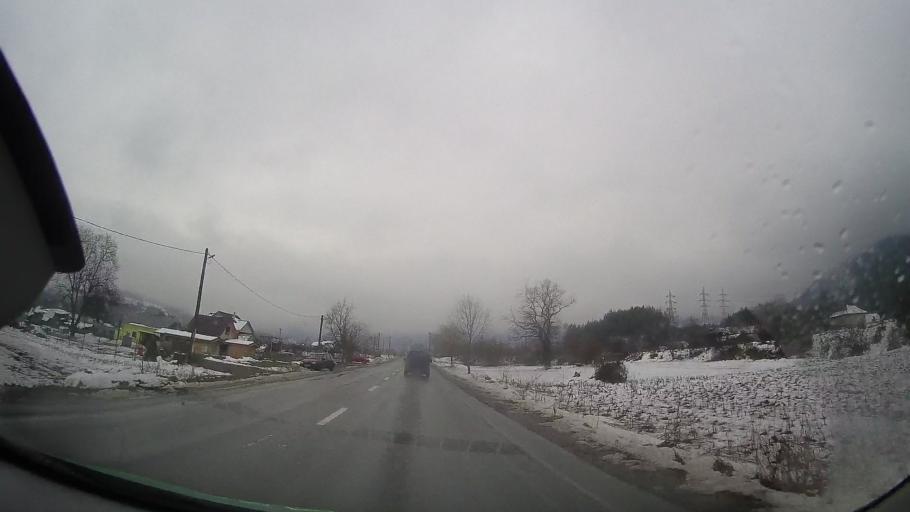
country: RO
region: Neamt
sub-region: Comuna Pangarati
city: Stejaru
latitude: 46.9256
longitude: 26.1921
